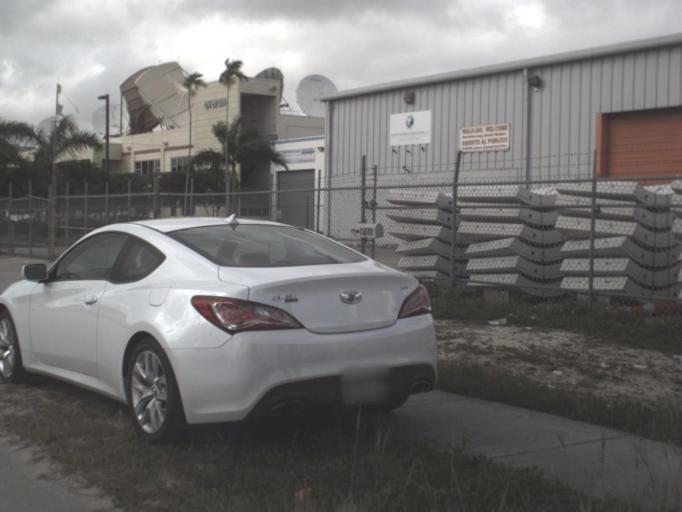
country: US
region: Florida
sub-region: Miami-Dade County
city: Hialeah Gardens
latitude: 25.8408
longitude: -80.3152
